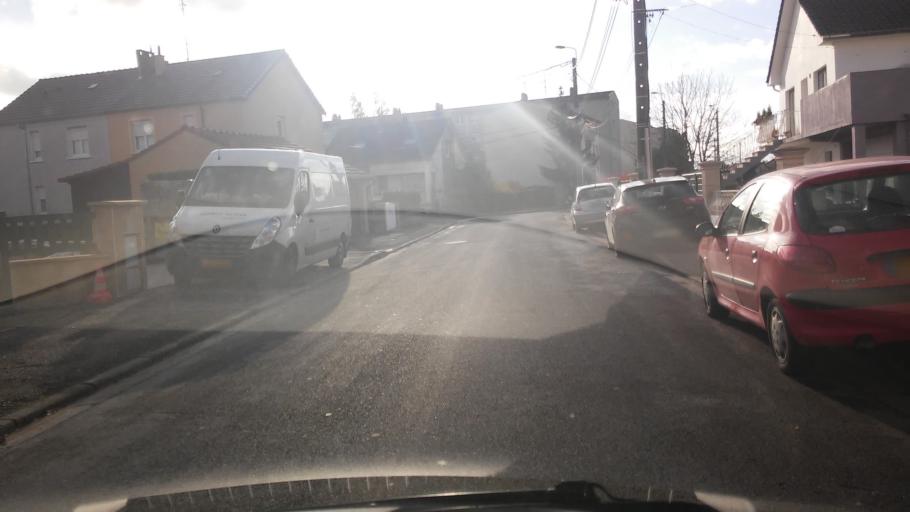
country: FR
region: Lorraine
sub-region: Departement de la Moselle
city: Talange
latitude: 49.2362
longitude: 6.1646
